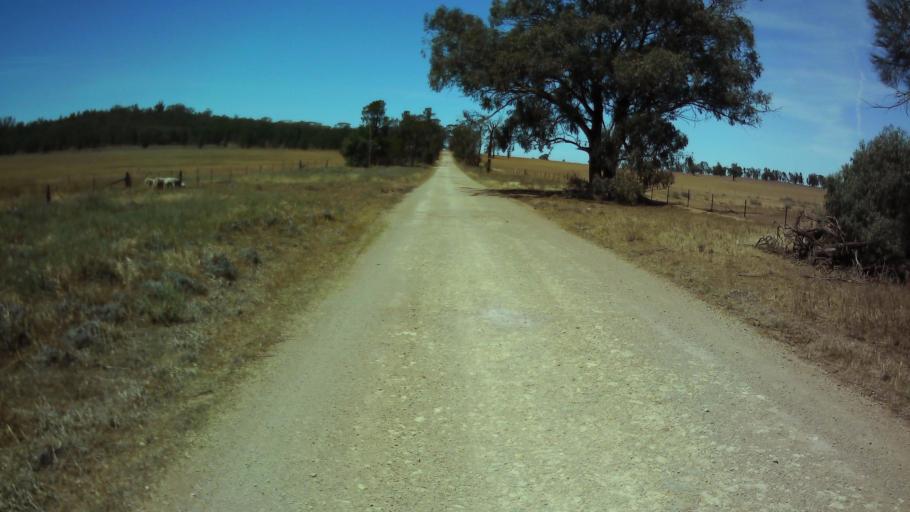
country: AU
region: New South Wales
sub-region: Forbes
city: Forbes
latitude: -33.7071
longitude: 147.7005
